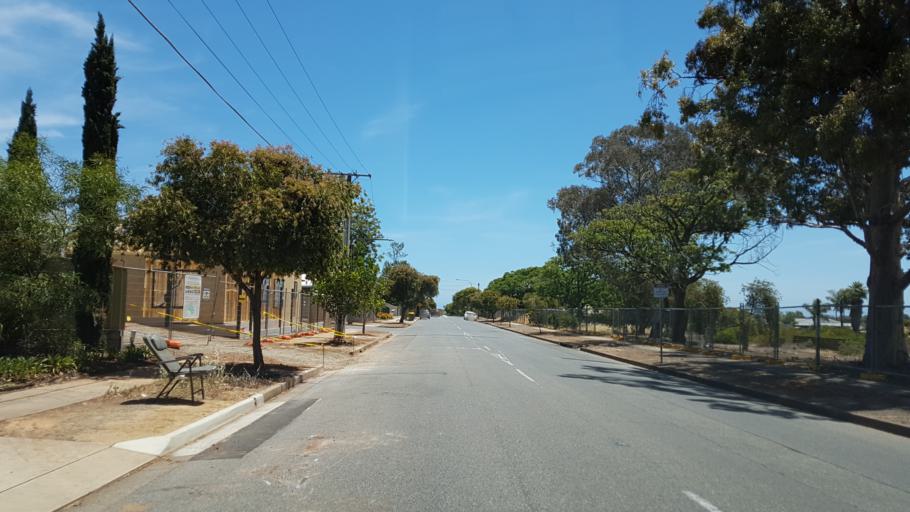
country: AU
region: South Australia
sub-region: Holdfast Bay
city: Seacliff Park
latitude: -35.0256
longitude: 138.5347
